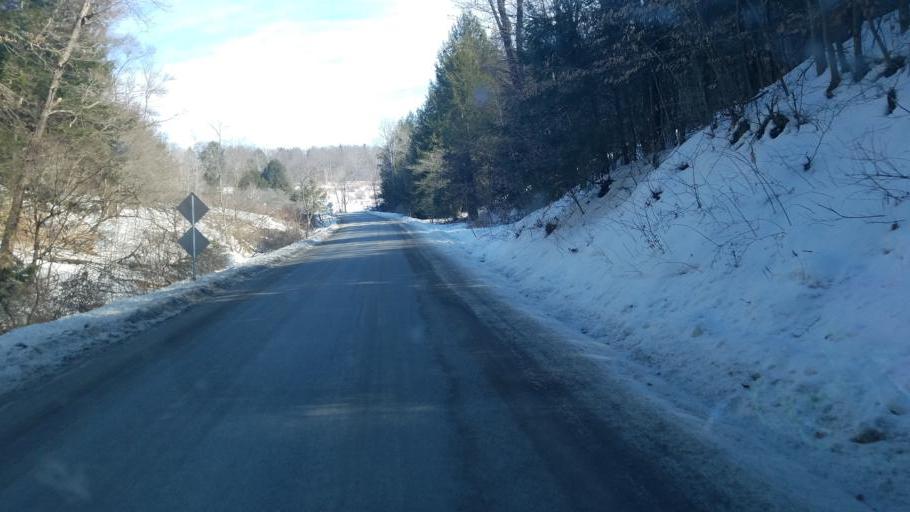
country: US
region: New York
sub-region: Allegany County
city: Andover
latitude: 42.0527
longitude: -77.7784
